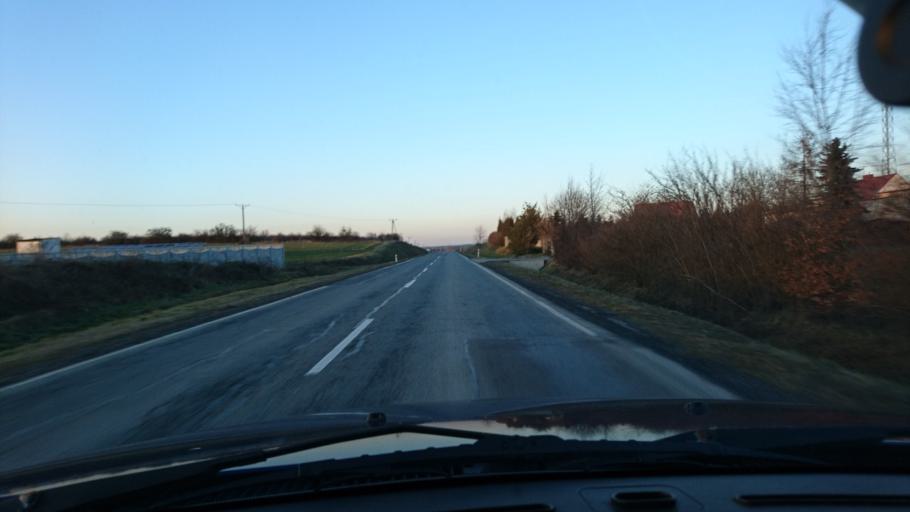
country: PL
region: Silesian Voivodeship
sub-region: Powiat gliwicki
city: Wielowies
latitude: 50.5060
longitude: 18.6045
